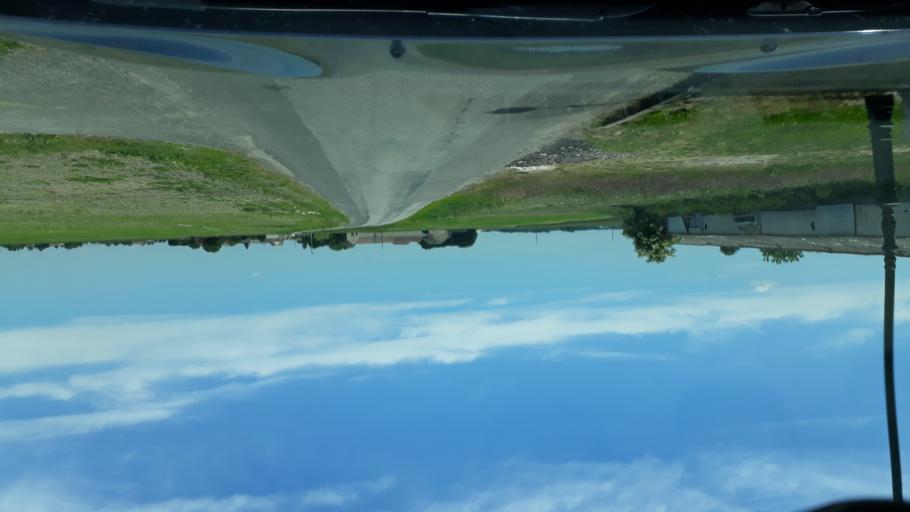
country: FR
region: Centre
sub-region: Departement du Loiret
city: Dadonville
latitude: 48.1021
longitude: 2.2684
